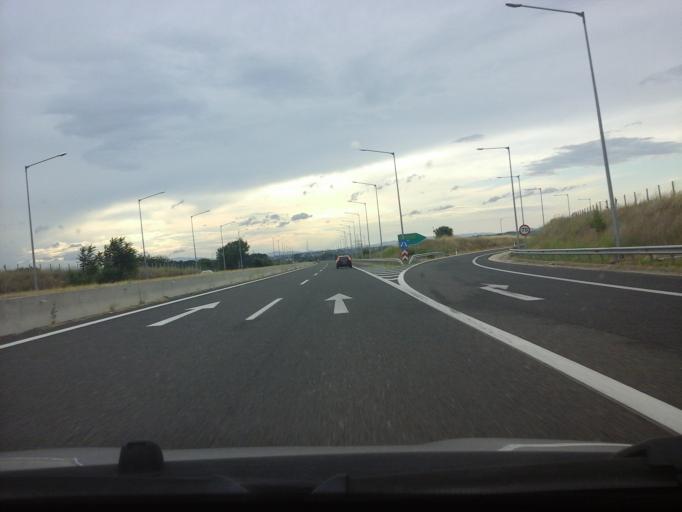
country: GR
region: East Macedonia and Thrace
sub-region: Nomos Rodopis
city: Komotini
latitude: 41.1028
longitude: 25.3560
